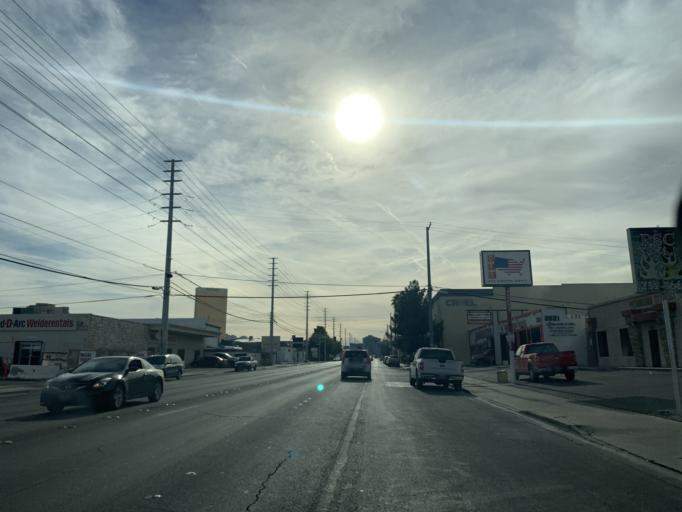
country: US
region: Nevada
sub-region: Clark County
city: Las Vegas
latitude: 36.1425
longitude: -115.1698
